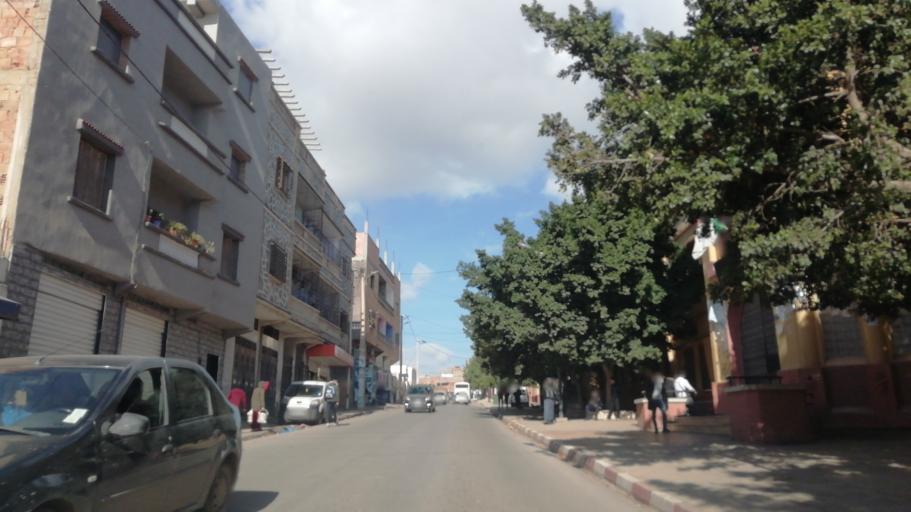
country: DZ
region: Oran
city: Es Senia
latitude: 35.6370
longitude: -0.6643
